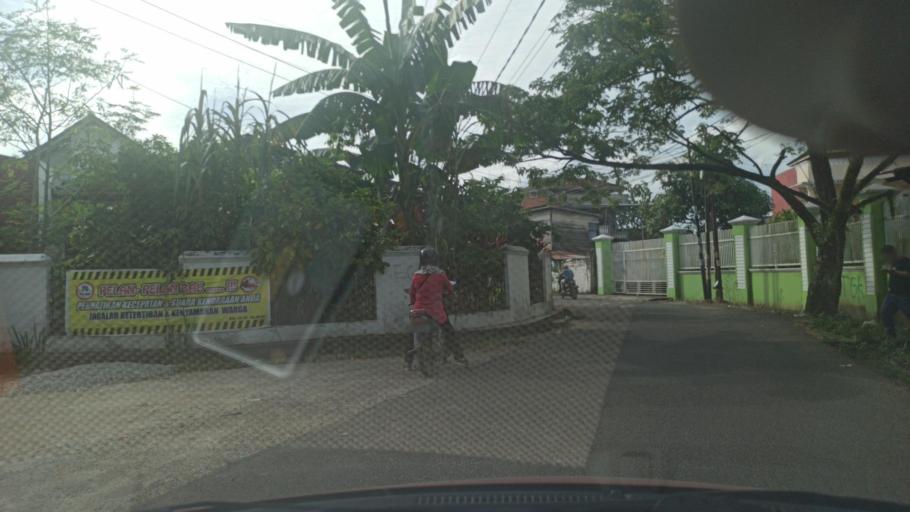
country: ID
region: South Sumatra
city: Plaju
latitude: -2.9926
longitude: 104.7250
